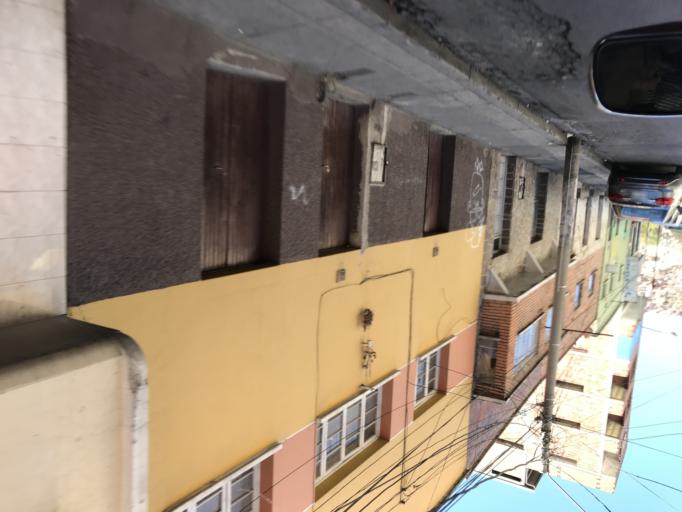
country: BO
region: La Paz
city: La Paz
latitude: -16.4945
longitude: -68.1510
